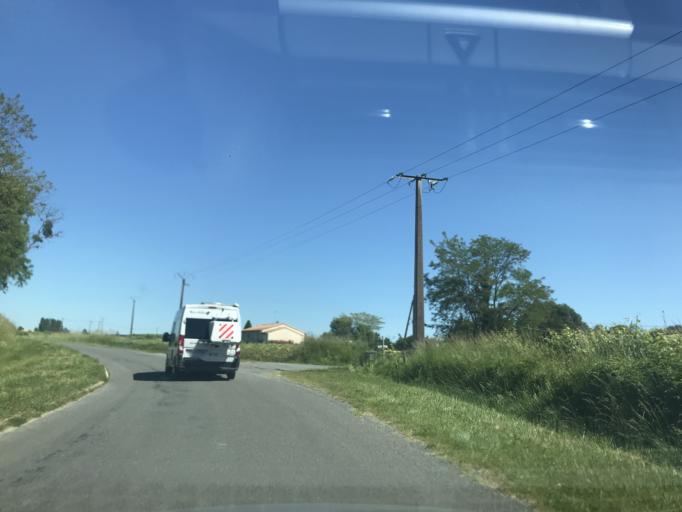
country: FR
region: Poitou-Charentes
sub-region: Departement de la Charente-Maritime
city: Mortagne-sur-Gironde
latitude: 45.4220
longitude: -0.7147
